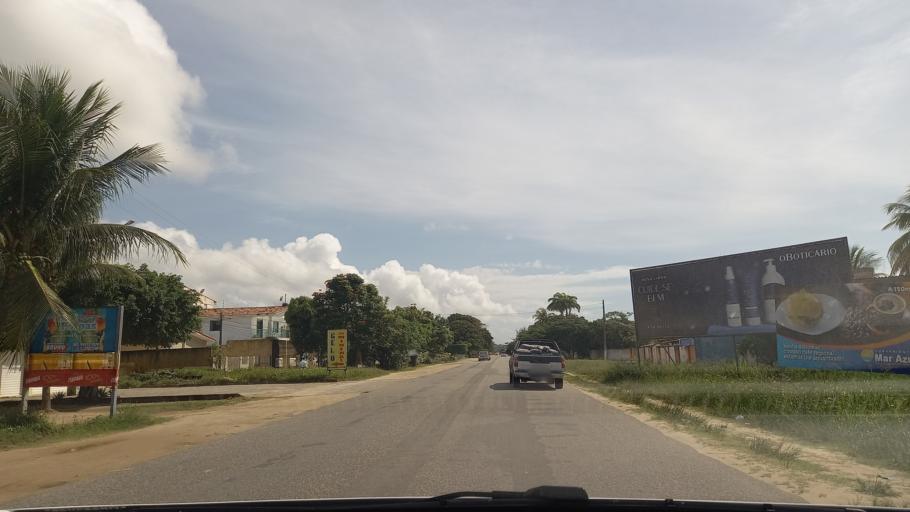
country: BR
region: Pernambuco
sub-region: Sao Jose Da Coroa Grande
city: Sao Jose da Coroa Grande
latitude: -8.9025
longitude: -35.1514
